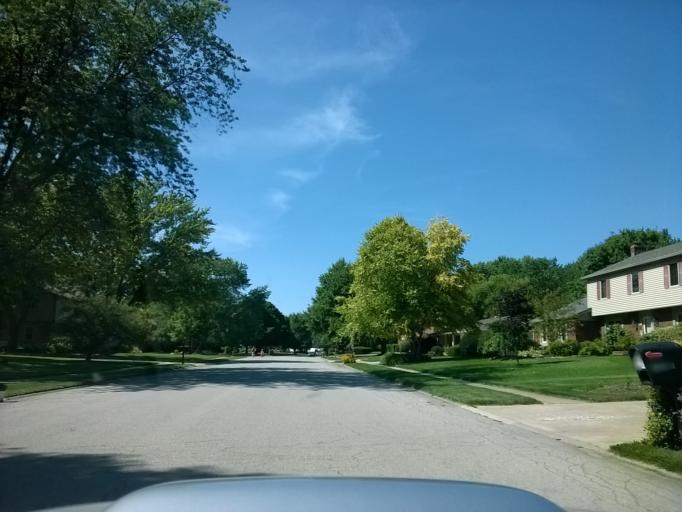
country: US
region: Indiana
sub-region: Hamilton County
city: Carmel
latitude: 39.9461
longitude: -86.1032
